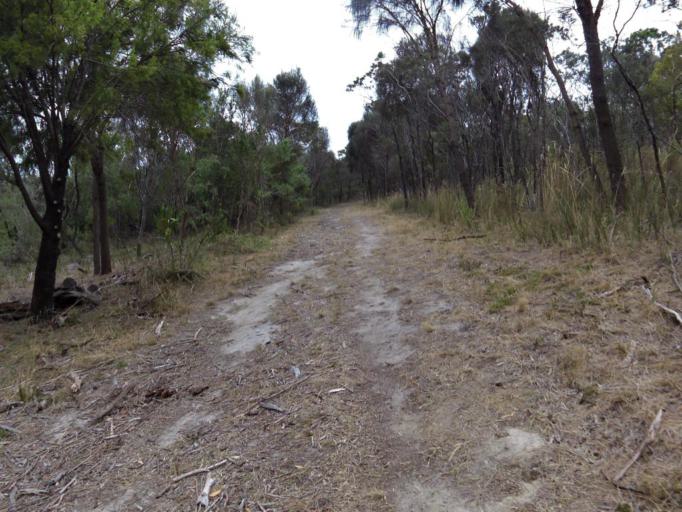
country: AU
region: Victoria
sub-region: Mornington Peninsula
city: Safety Beach
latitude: -38.2920
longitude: 144.9990
